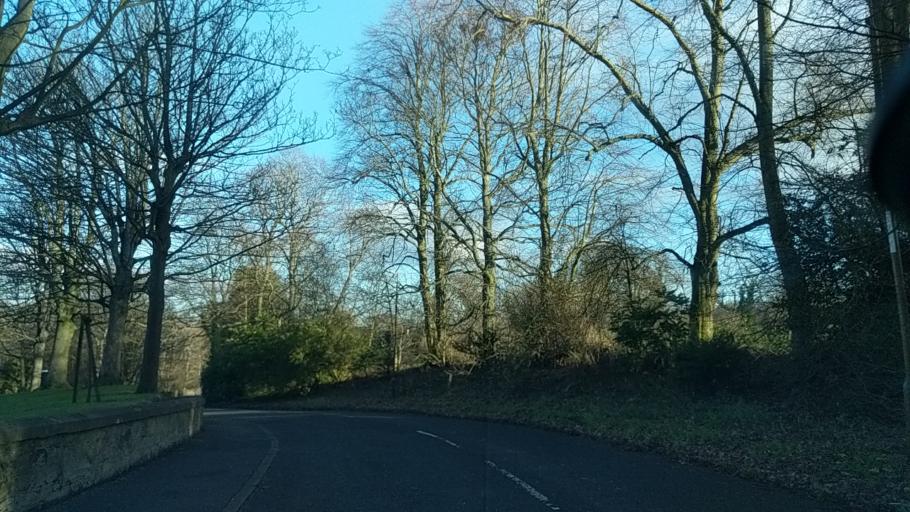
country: GB
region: Scotland
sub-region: West Lothian
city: Broxburn
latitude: 55.9772
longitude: -3.5259
